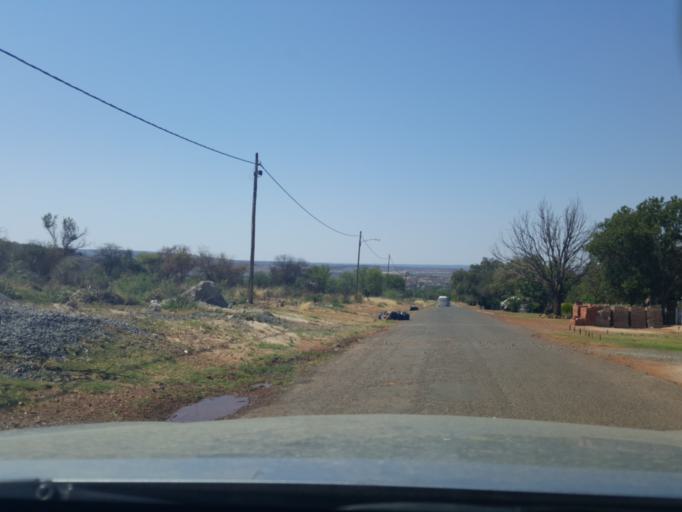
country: ZA
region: North-West
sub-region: Ngaka Modiri Molema District Municipality
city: Zeerust
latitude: -25.5320
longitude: 26.0815
